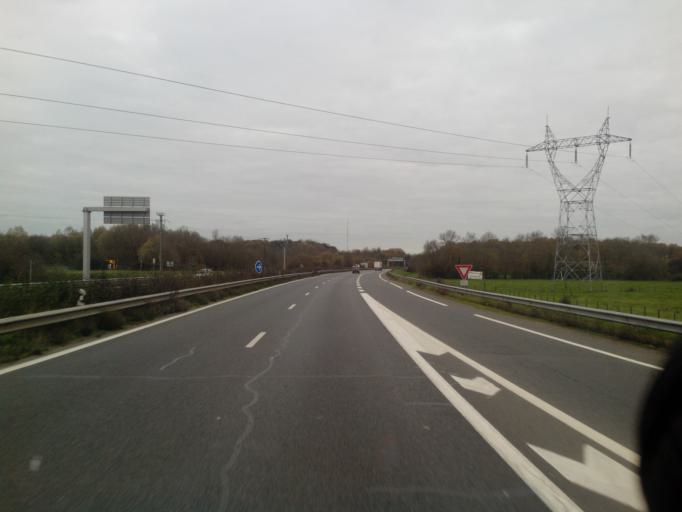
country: FR
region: Pays de la Loire
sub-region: Departement de la Loire-Atlantique
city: Basse-Goulaine
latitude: 47.2162
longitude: -1.4531
